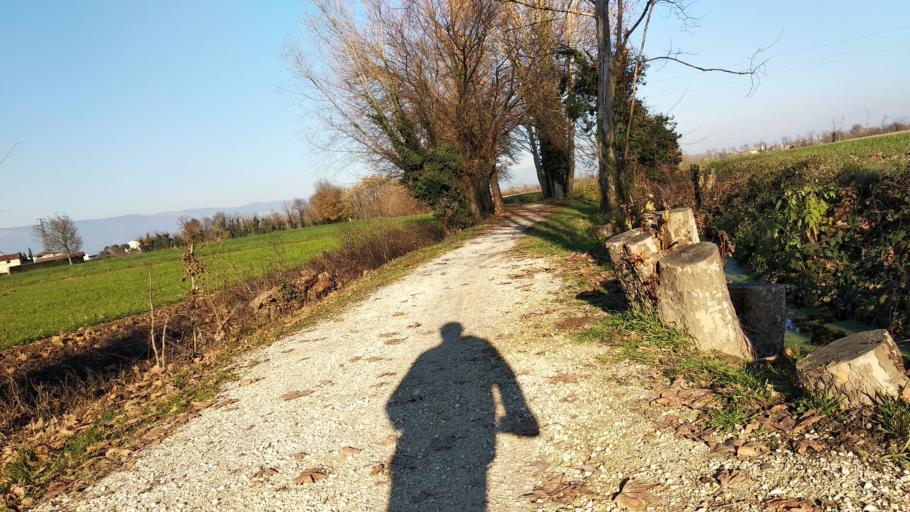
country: IT
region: Veneto
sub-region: Provincia di Vicenza
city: Crispi Cavour
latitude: 45.5818
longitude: 11.5375
